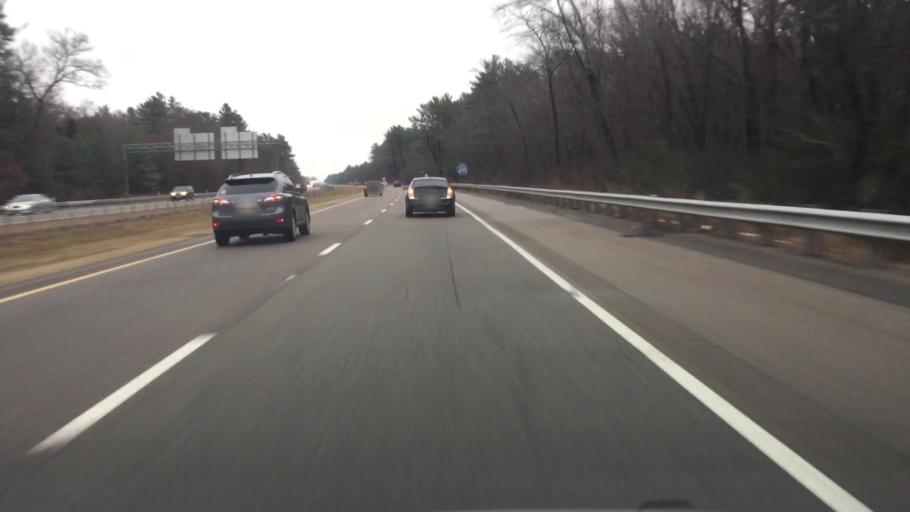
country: US
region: Massachusetts
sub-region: Plymouth County
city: Middleborough Center
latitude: 41.8969
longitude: -70.9560
